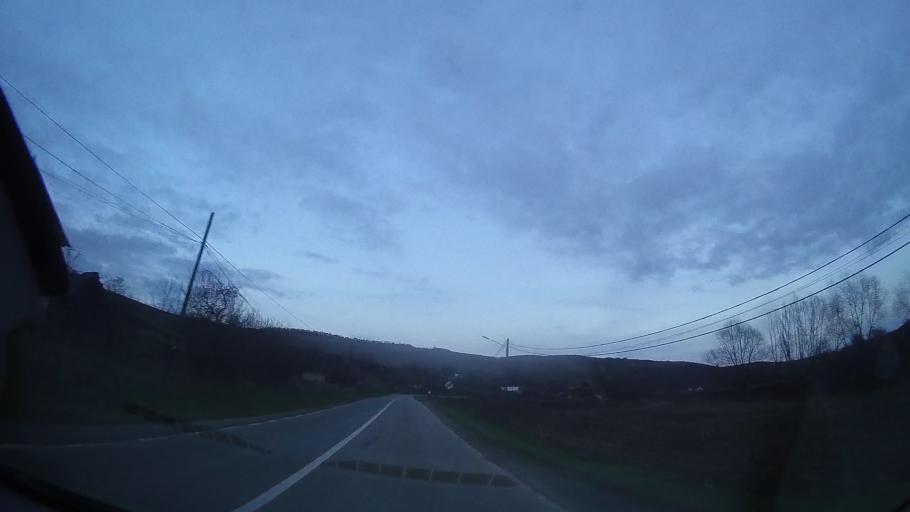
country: RO
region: Cluj
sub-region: Comuna Caianu
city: Vaida-Camaras
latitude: 46.8054
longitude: 23.9630
